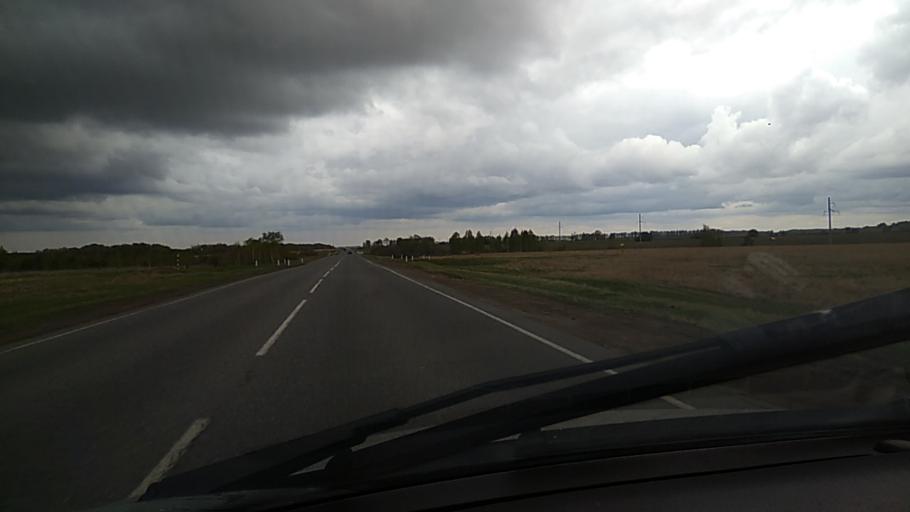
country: RU
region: Kurgan
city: Dalmatovo
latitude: 56.2897
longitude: 62.8486
